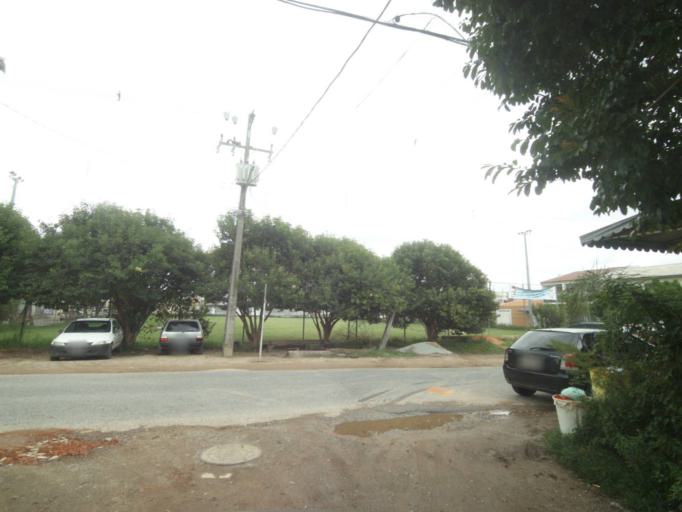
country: BR
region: Parana
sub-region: Pinhais
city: Pinhais
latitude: -25.4523
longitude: -49.1986
